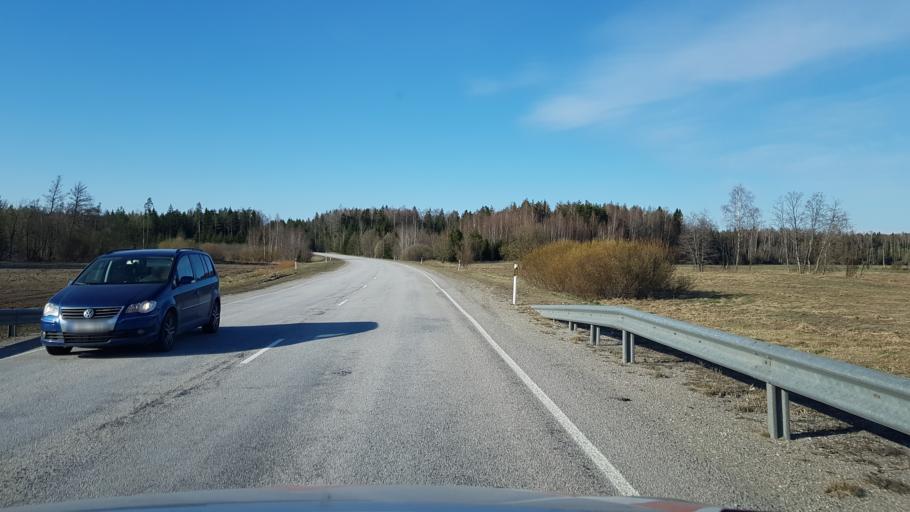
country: EE
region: Ida-Virumaa
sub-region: Johvi vald
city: Johvi
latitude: 59.1497
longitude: 27.3592
